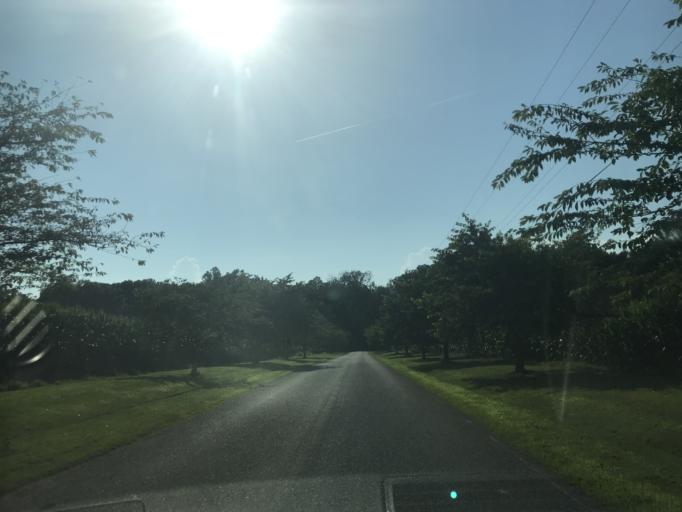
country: US
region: Maryland
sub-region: Harford County
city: Havre de Grace
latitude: 39.5223
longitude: -76.1203
